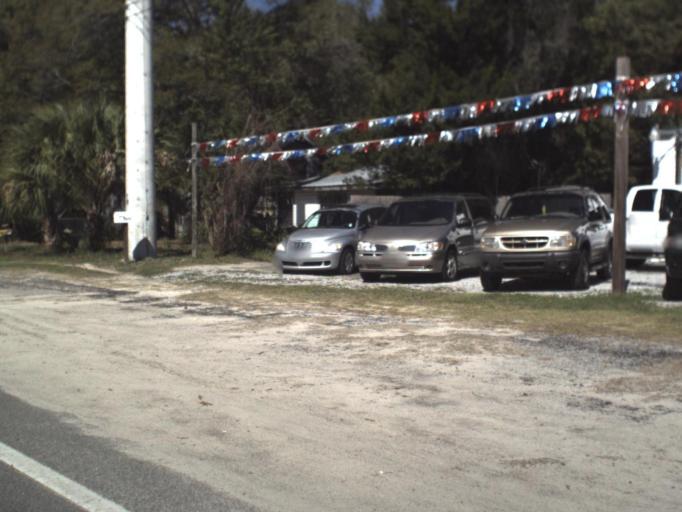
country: US
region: Florida
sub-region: Bay County
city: Springfield
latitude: 30.1531
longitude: -85.6007
